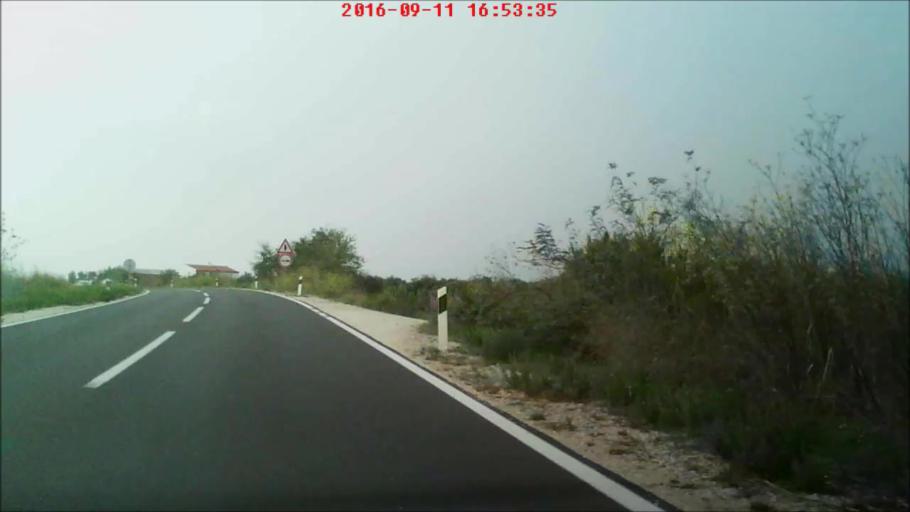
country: HR
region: Zadarska
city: Nin
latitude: 44.2489
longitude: 15.1644
